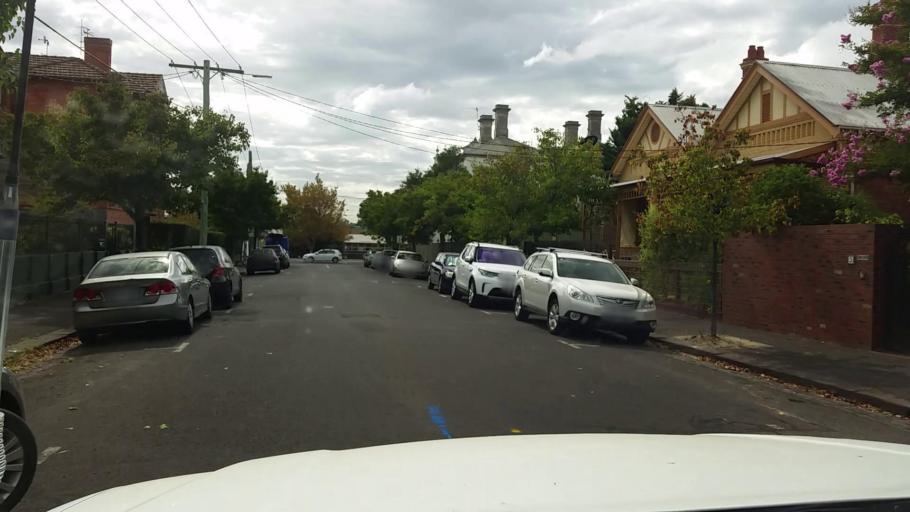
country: AU
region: Victoria
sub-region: Port Phillip
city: Saint Kilda
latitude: -37.8701
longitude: 144.9870
